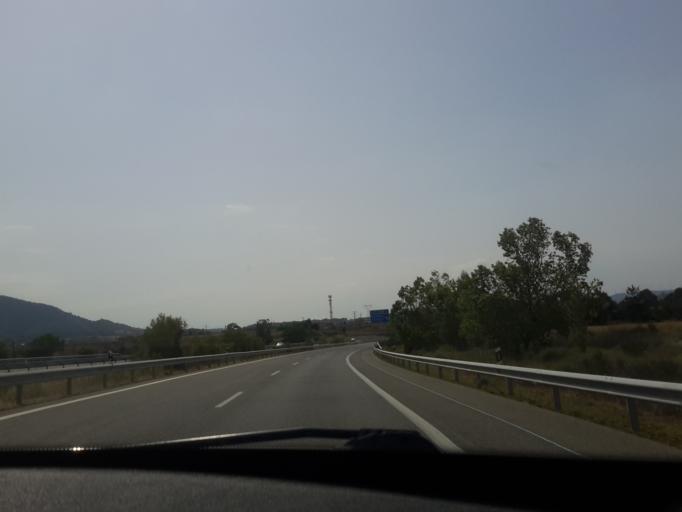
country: ES
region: Catalonia
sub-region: Provincia de Tarragona
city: Montblanc
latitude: 41.3870
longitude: 1.1770
